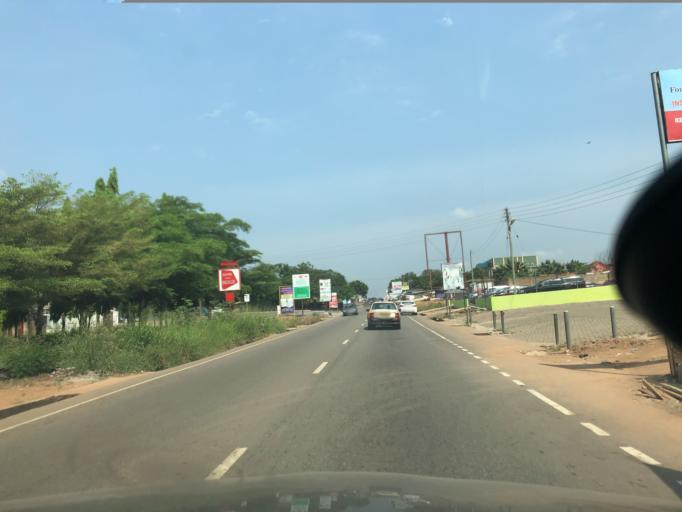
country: GH
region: Greater Accra
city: Medina Estates
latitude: 5.6790
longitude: -0.1921
